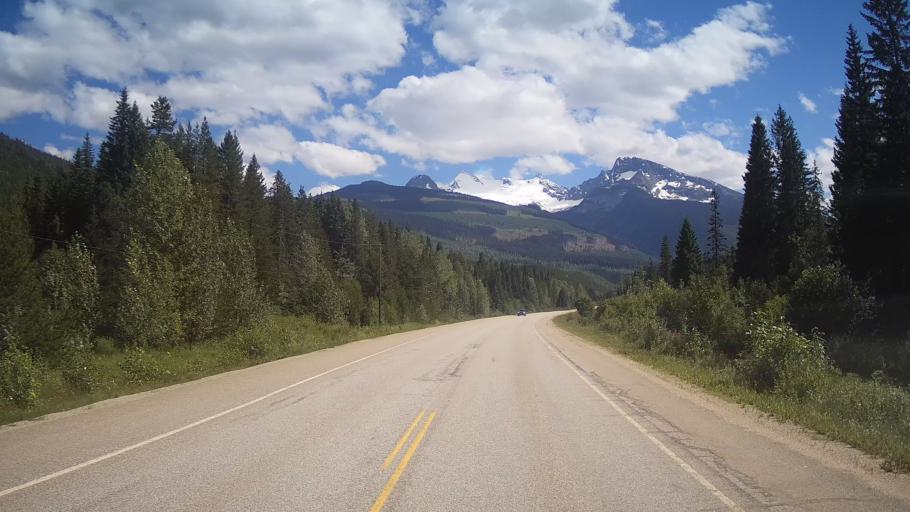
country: CA
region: Alberta
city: Jasper Park Lodge
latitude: 52.5955
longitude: -119.1026
